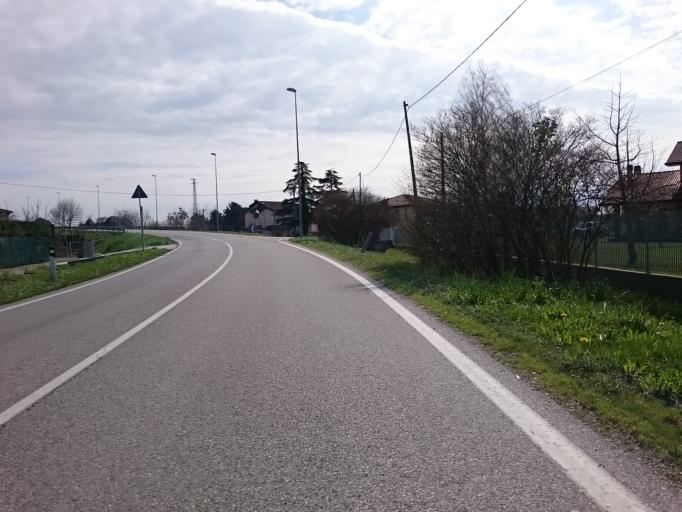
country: IT
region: Veneto
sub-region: Provincia di Padova
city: Mandriola-Sant'Agostino
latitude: 45.3489
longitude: 11.8479
